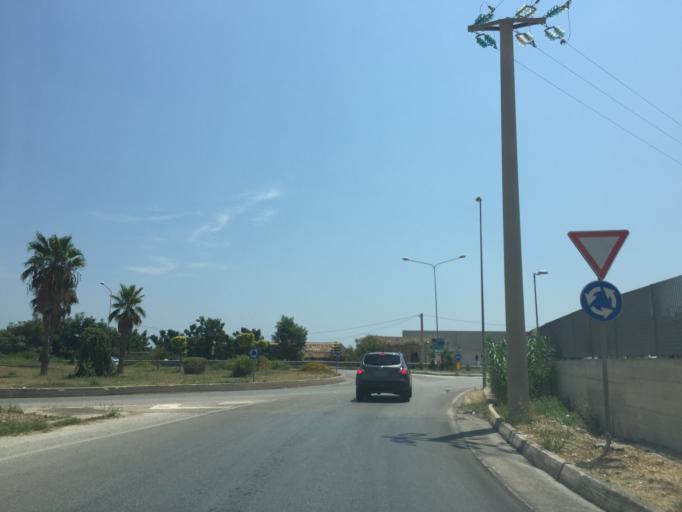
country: IT
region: Sicily
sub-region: Provincia di Siracusa
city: Avola
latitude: 36.9201
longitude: 15.1466
